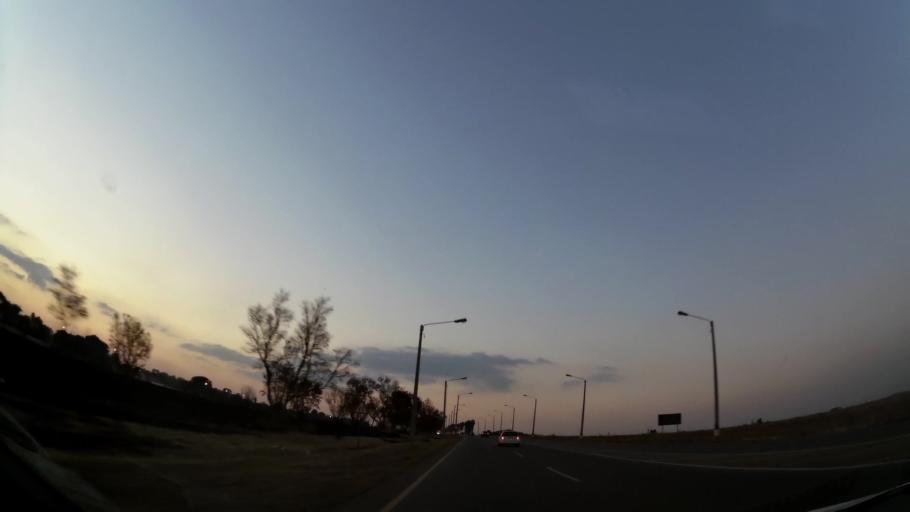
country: ZA
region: Gauteng
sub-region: Ekurhuleni Metropolitan Municipality
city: Springs
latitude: -26.3139
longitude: 28.4554
